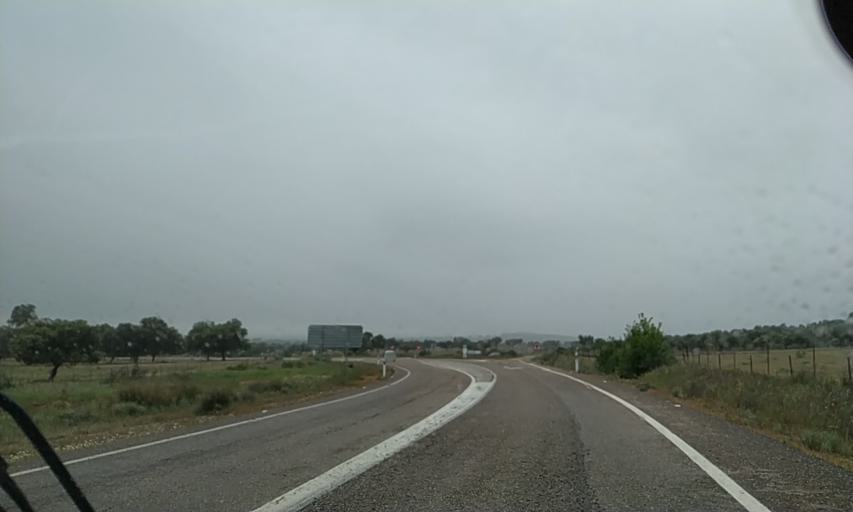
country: ES
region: Extremadura
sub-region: Provincia de Badajoz
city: La Roca de la Sierra
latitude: 39.1087
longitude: -6.7066
